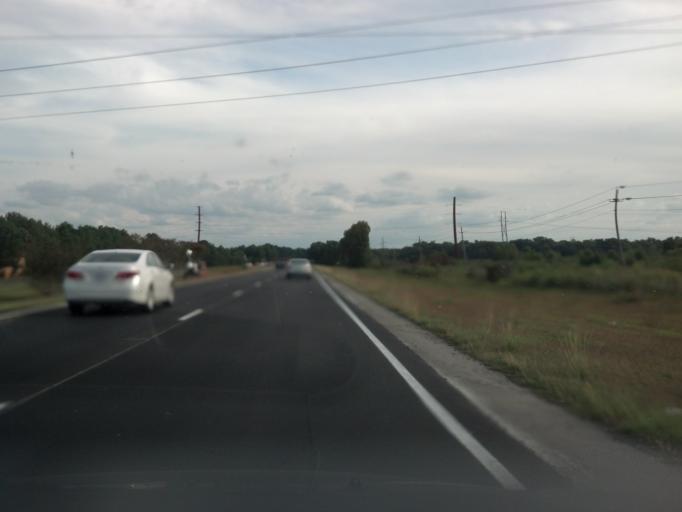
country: US
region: North Carolina
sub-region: Pitt County
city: Greenville
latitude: 35.6202
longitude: -77.3291
